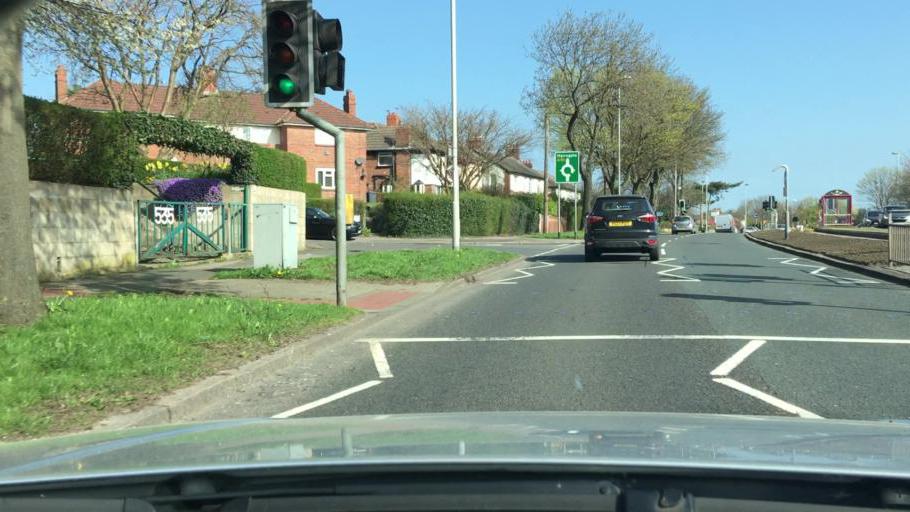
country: GB
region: England
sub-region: City and Borough of Leeds
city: Chapel Allerton
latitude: 53.8272
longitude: -1.5471
